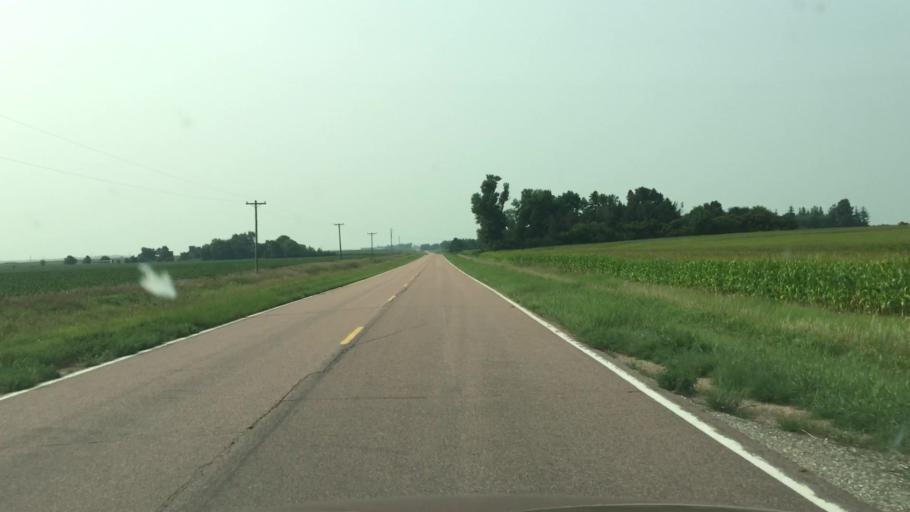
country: US
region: Iowa
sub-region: O'Brien County
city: Sheldon
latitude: 43.2513
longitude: -95.7832
